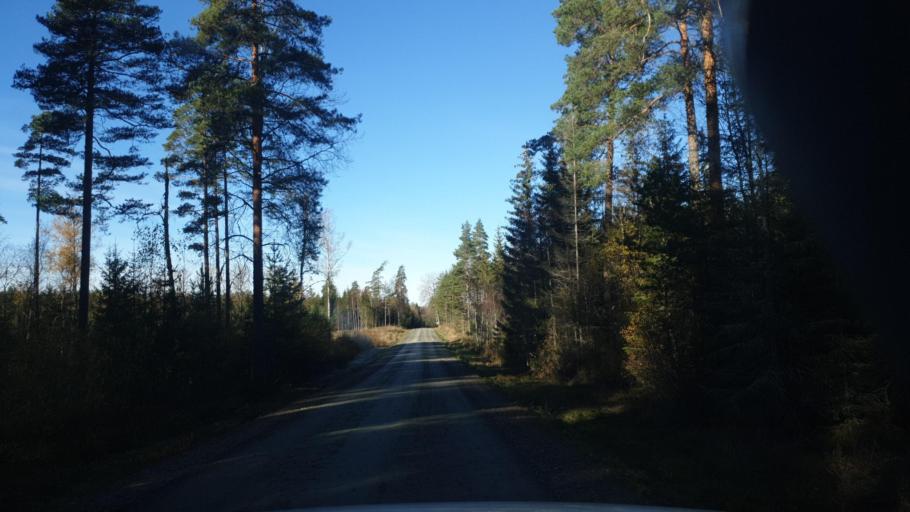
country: SE
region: Vaermland
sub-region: Karlstads Kommun
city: Edsvalla
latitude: 59.4478
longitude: 13.1129
